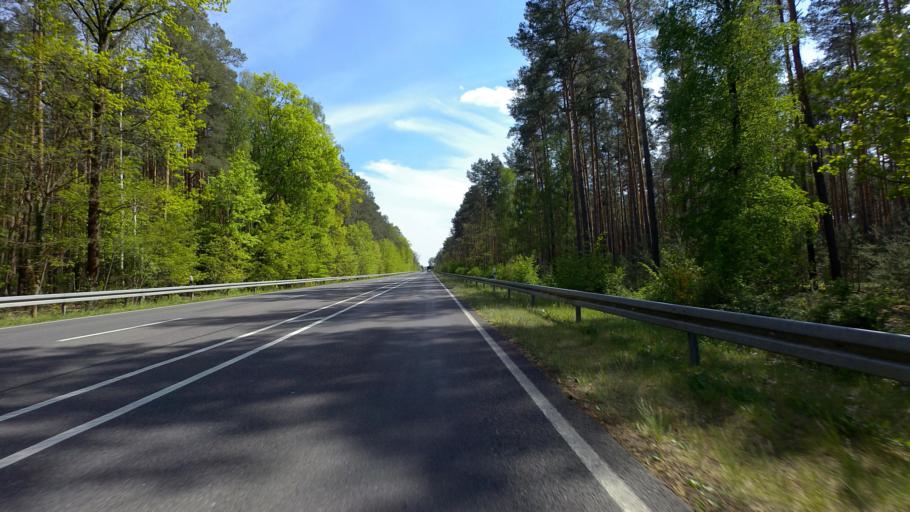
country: DE
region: Brandenburg
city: Heinersbruck
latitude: 51.6916
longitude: 14.4985
